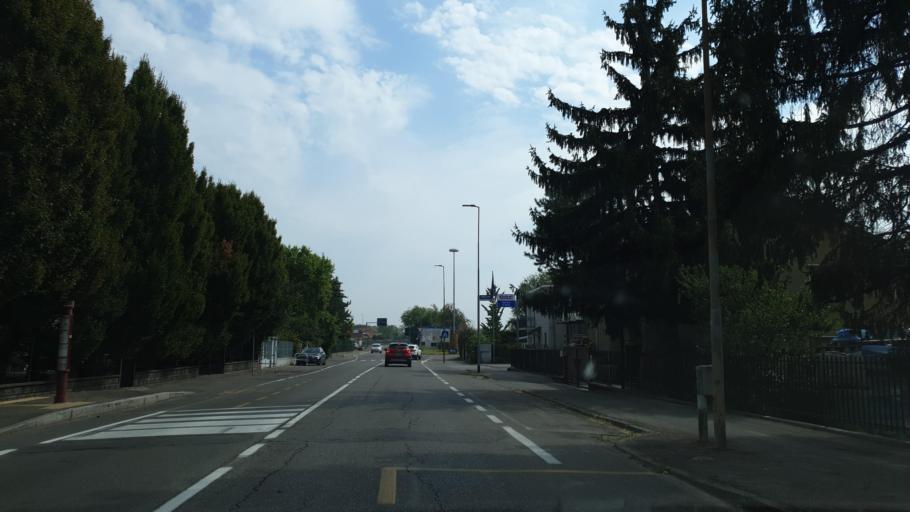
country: IT
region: Emilia-Romagna
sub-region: Provincia di Parma
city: Vicofertile
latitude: 44.8171
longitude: 10.2878
